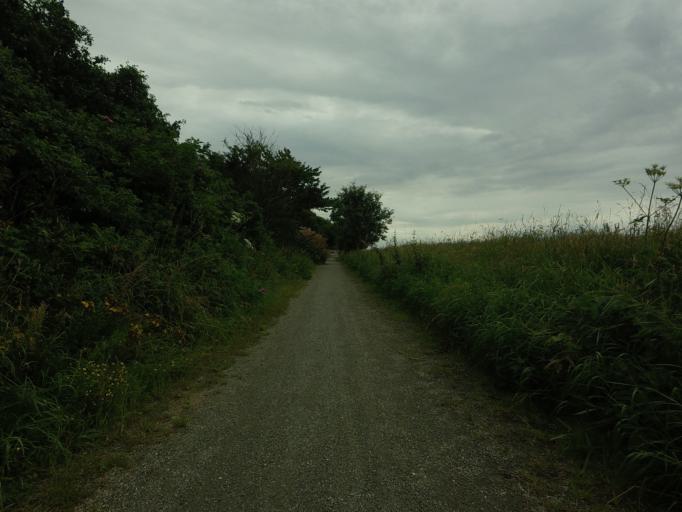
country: DK
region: North Denmark
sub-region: Alborg Kommune
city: Vadum
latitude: 57.1125
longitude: 9.8816
